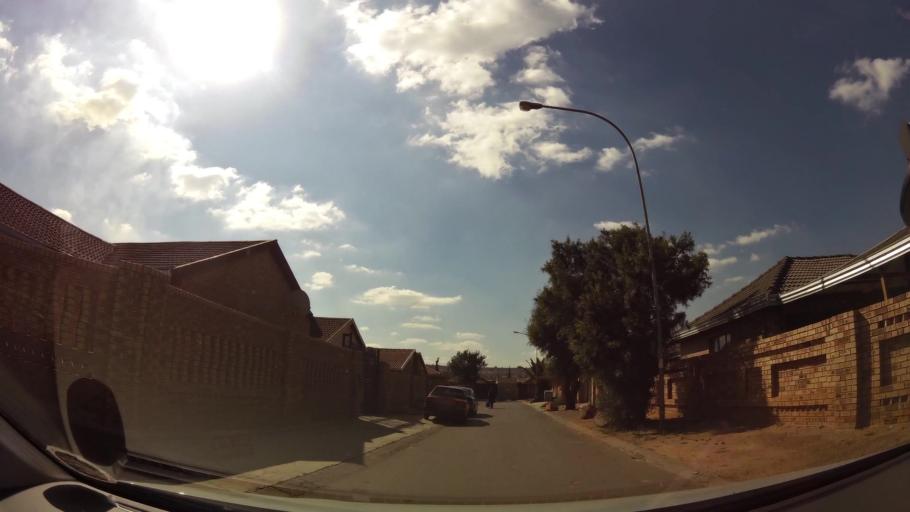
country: ZA
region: Gauteng
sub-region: City of Johannesburg Metropolitan Municipality
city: Roodepoort
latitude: -26.2102
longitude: 27.8718
